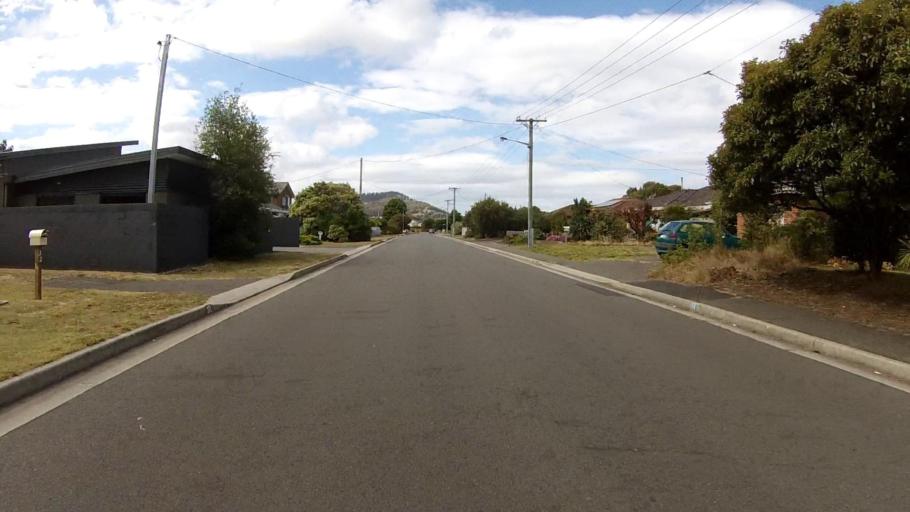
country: AU
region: Tasmania
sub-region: Clarence
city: Lauderdale
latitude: -42.9020
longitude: 147.4930
